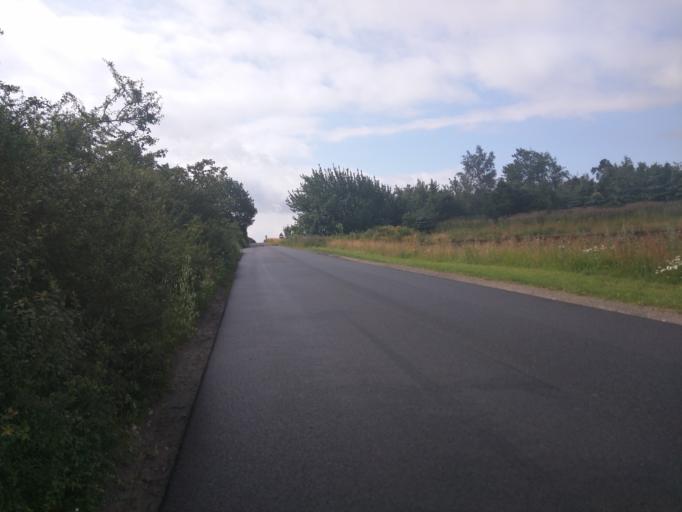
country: DK
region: Zealand
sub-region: Kalundborg Kommune
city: Svebolle
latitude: 55.6775
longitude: 11.3119
